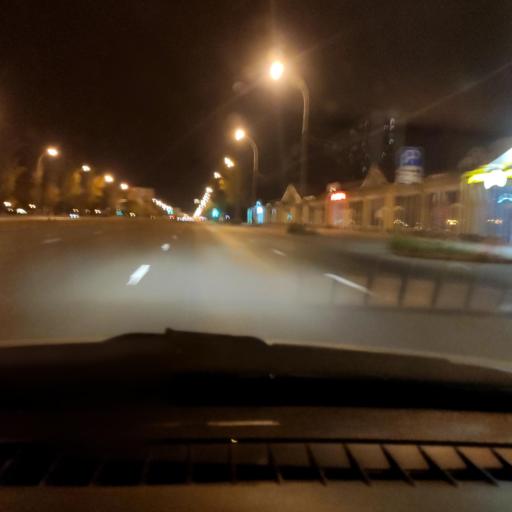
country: RU
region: Samara
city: Tol'yatti
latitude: 53.5227
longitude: 49.2803
